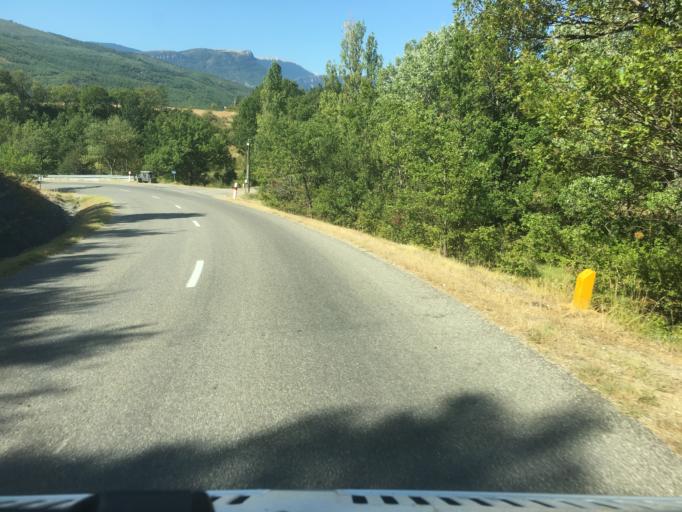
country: FR
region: Provence-Alpes-Cote d'Azur
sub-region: Departement des Alpes-de-Haute-Provence
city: Sisteron
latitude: 44.1783
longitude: 5.9257
